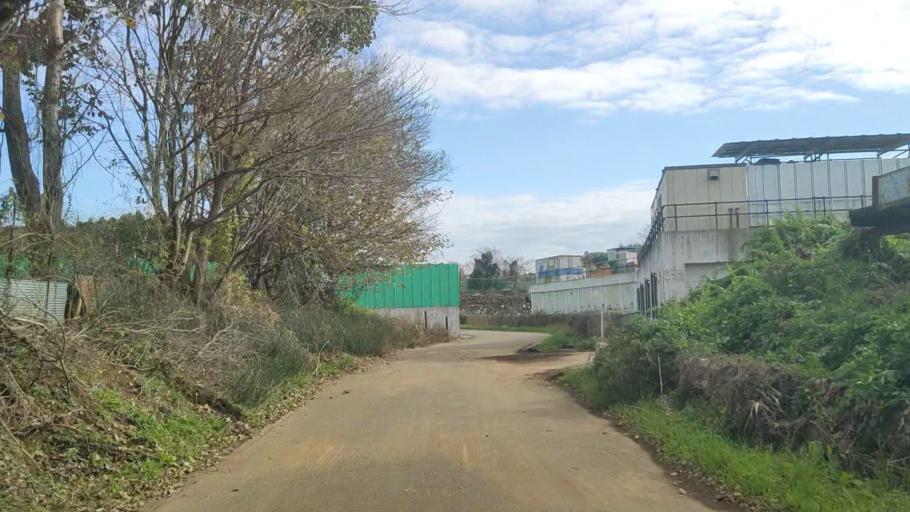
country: JP
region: Kanagawa
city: Minami-rinkan
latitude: 35.4871
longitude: 139.4943
